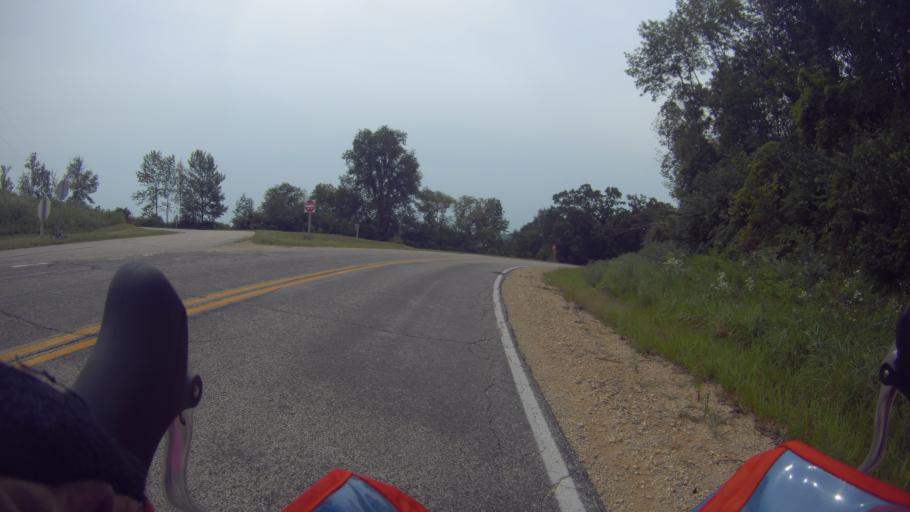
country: US
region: Wisconsin
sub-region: Dane County
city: Mount Horeb
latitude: 42.9240
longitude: -89.6772
